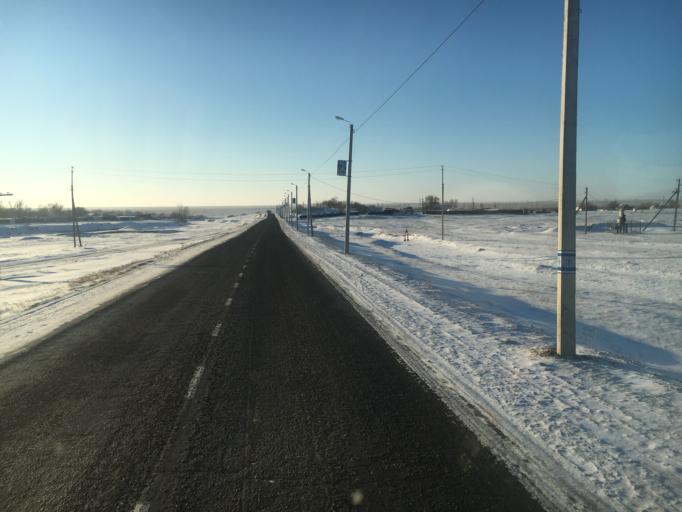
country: KZ
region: Aqtoebe
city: Khromtau
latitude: 50.1256
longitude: 59.1012
